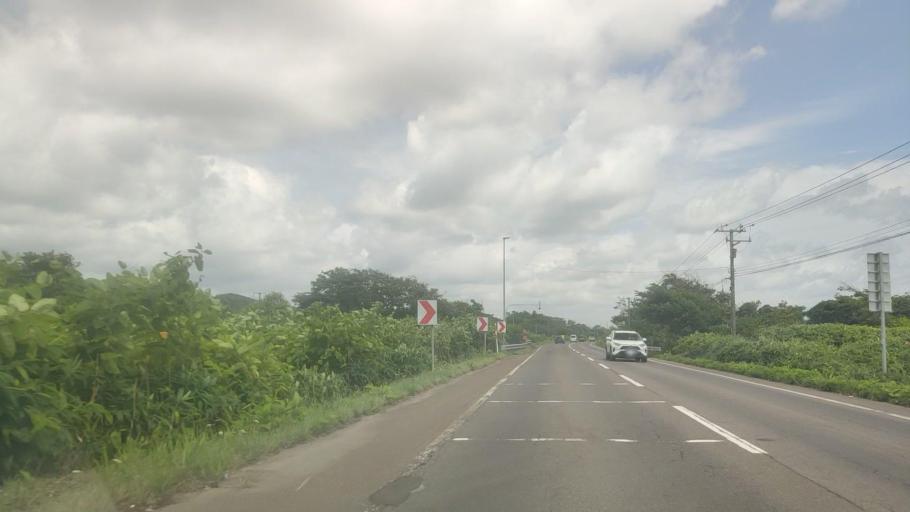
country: JP
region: Hokkaido
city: Niseko Town
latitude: 42.4574
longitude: 140.3341
